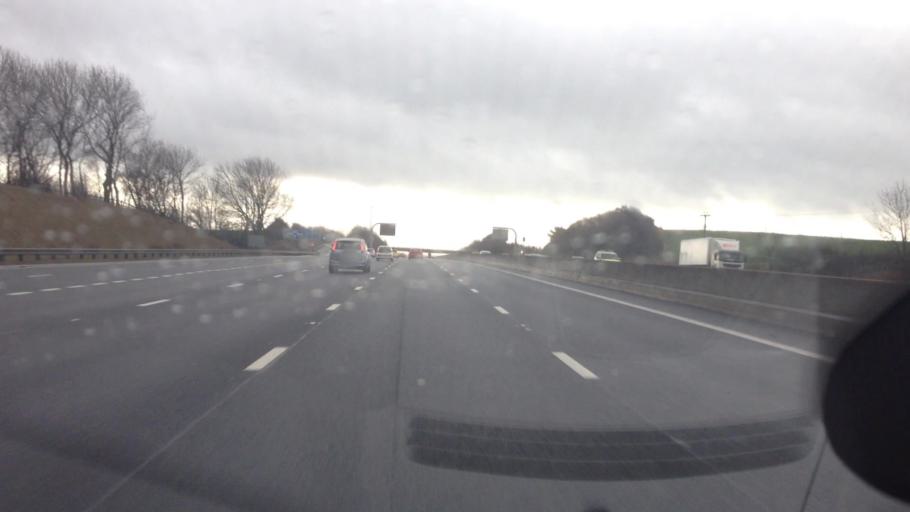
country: GB
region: England
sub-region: City and Borough of Wakefield
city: Ossett
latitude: 53.6883
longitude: -1.5561
